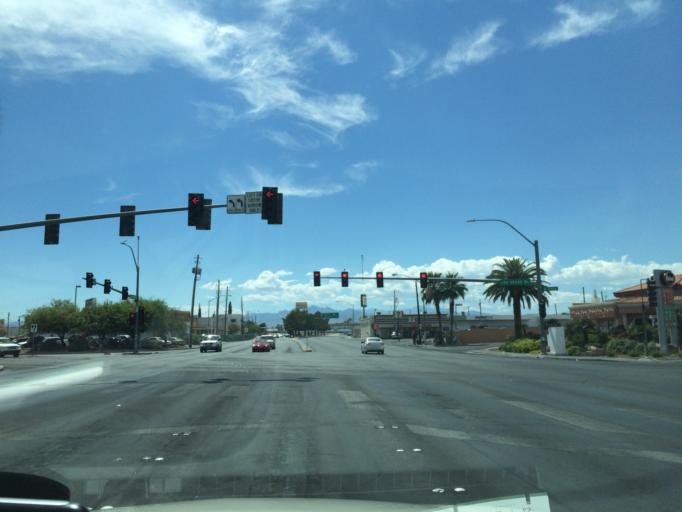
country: US
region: Nevada
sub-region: Clark County
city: North Las Vegas
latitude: 36.1958
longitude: -115.1286
